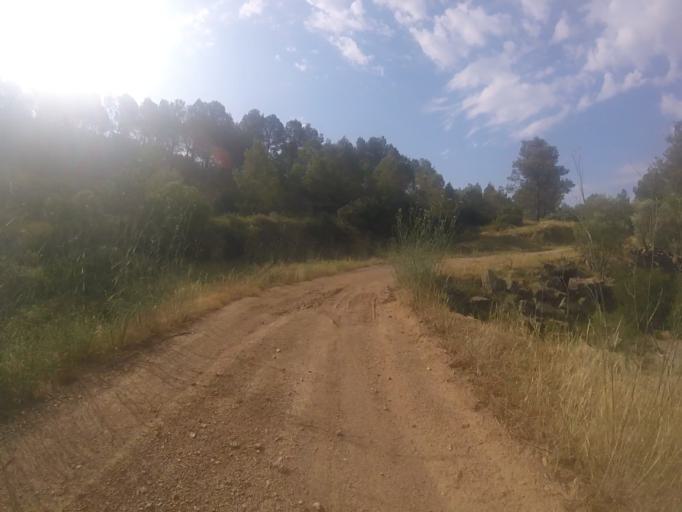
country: ES
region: Valencia
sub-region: Provincia de Castello
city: Cervera del Maestre
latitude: 40.3981
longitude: 0.2056
